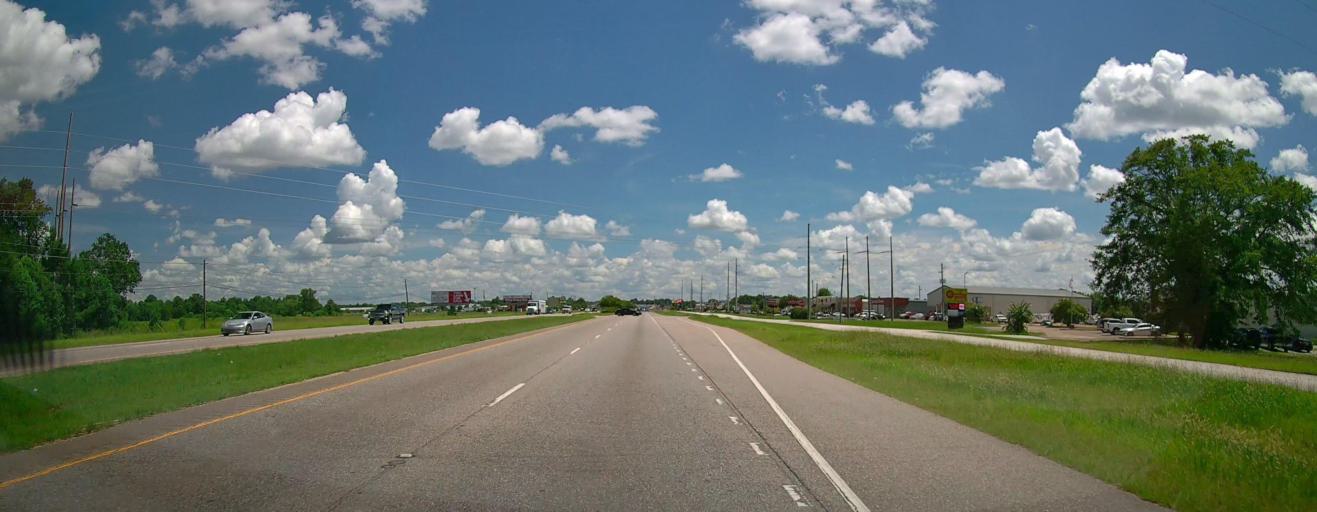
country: US
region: Alabama
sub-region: Elmore County
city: Blue Ridge
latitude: 32.4116
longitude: -86.2176
